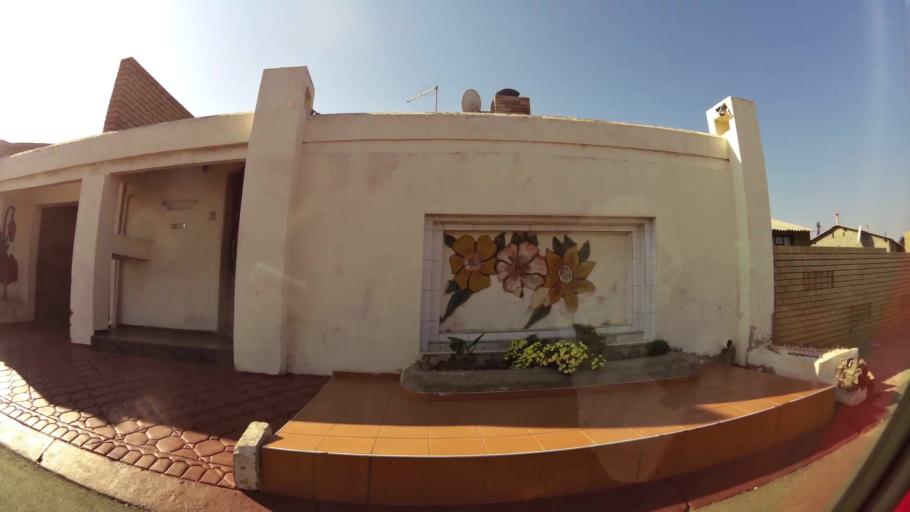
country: ZA
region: Gauteng
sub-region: City of Johannesburg Metropolitan Municipality
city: Soweto
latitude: -26.2486
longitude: 27.9532
